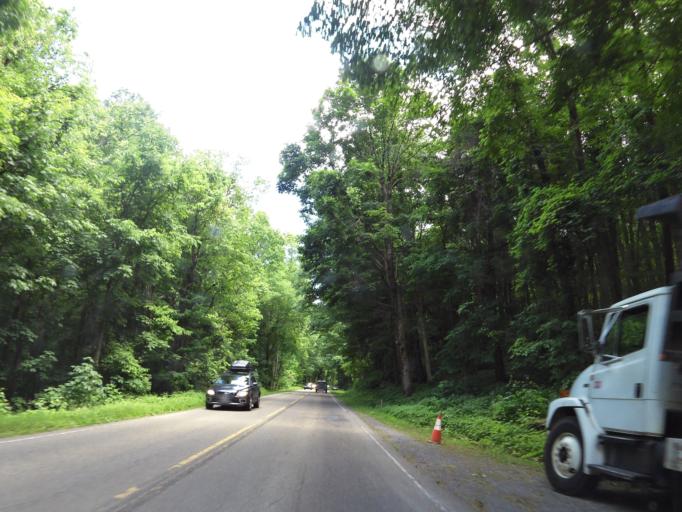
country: US
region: Tennessee
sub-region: Sevier County
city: Gatlinburg
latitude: 35.6437
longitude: -83.5075
